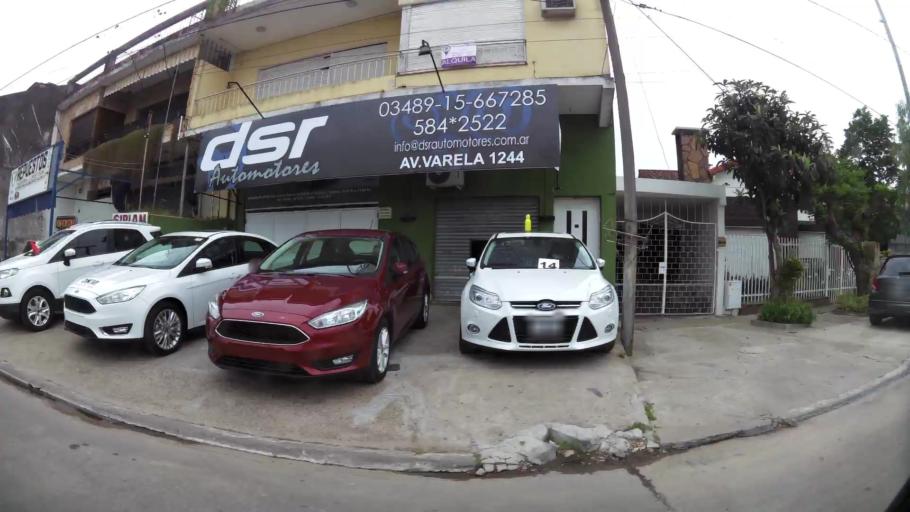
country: AR
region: Buenos Aires
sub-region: Partido de Campana
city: Campana
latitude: -34.1802
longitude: -58.9605
